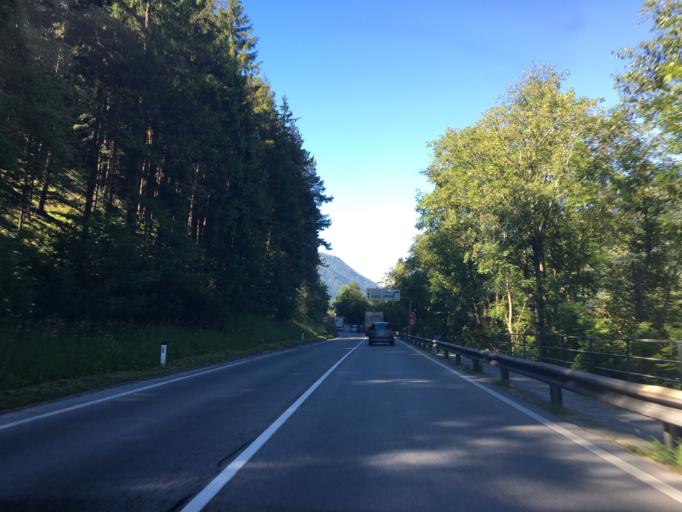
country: AT
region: Tyrol
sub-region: Politischer Bezirk Innsbruck Land
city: Fulpmes
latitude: 47.1522
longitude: 11.3557
